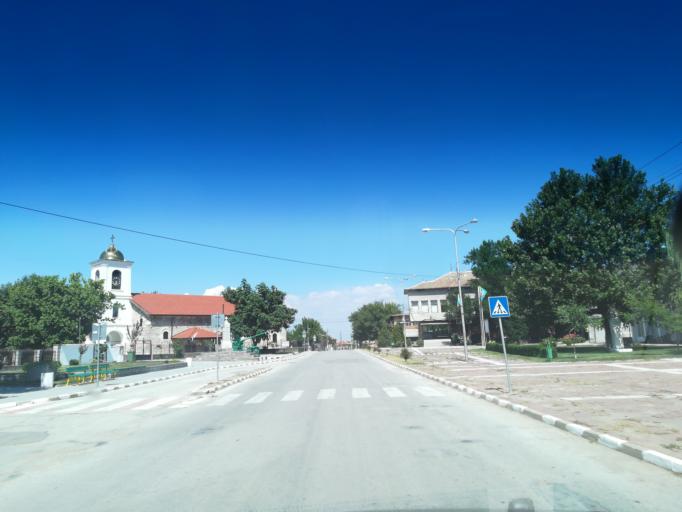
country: BG
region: Plovdiv
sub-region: Obshtina Sadovo
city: Sadovo
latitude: 42.0251
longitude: 25.1053
